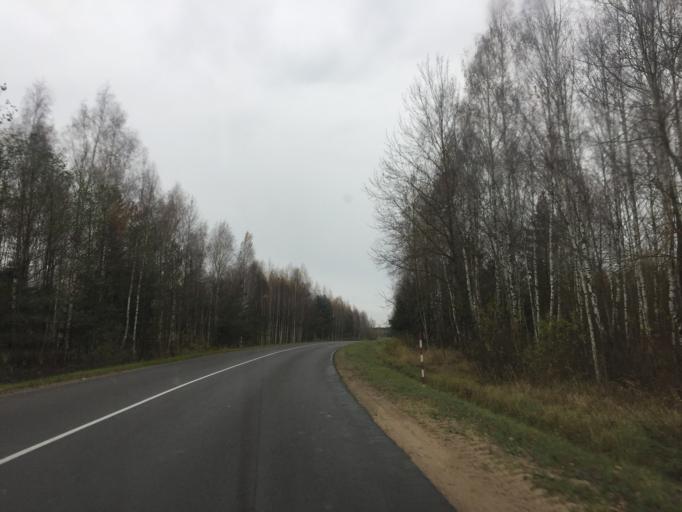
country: BY
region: Mogilev
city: Drybin
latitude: 54.1063
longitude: 31.1020
